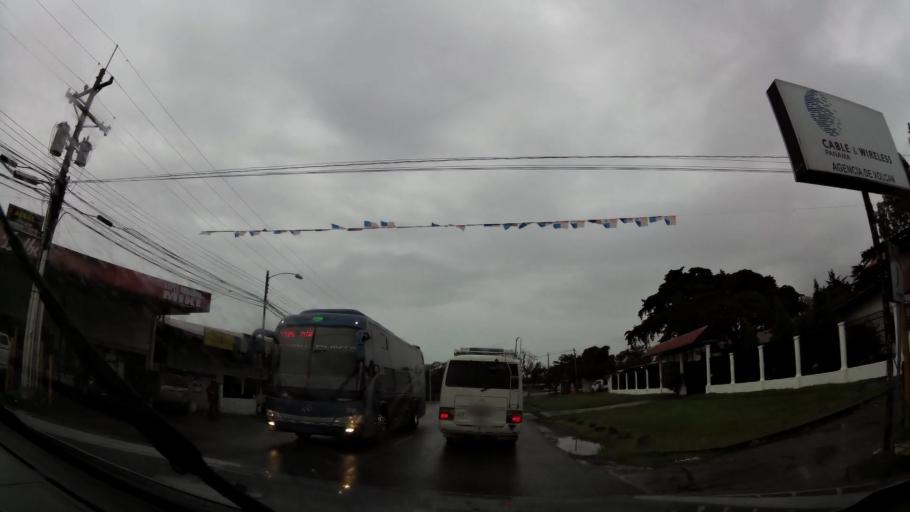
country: PA
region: Chiriqui
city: Volcan
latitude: 8.7796
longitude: -82.6437
